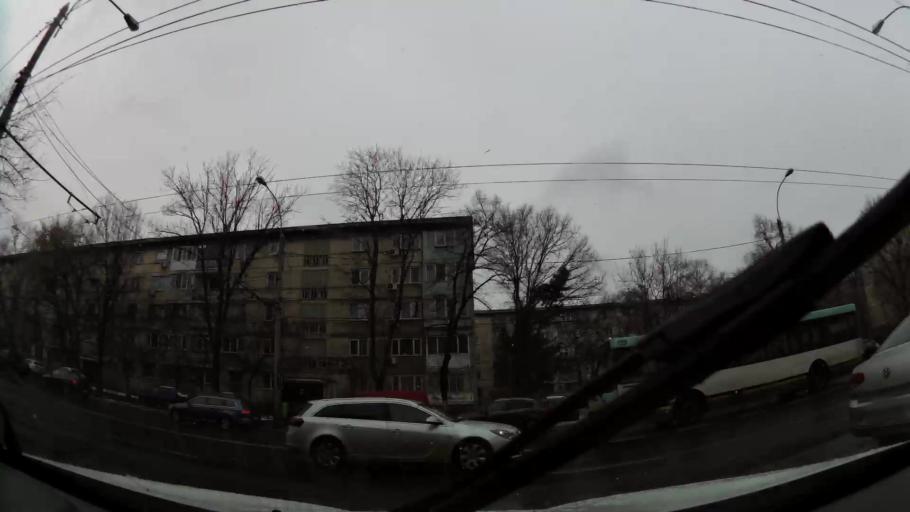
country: RO
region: Bucuresti
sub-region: Municipiul Bucuresti
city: Bucuresti
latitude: 44.4268
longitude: 26.0551
